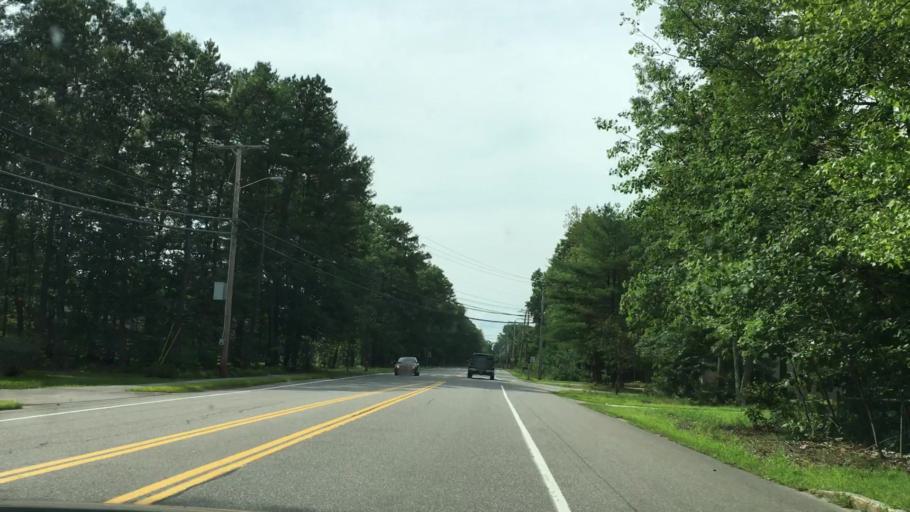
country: US
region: New Hampshire
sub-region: Merrimack County
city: East Concord
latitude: 43.2270
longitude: -71.5094
